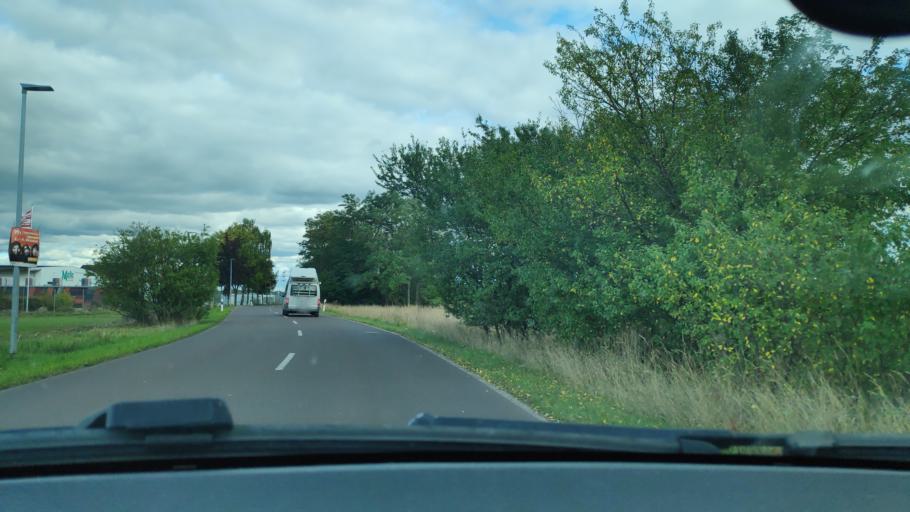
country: DE
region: Saxony-Anhalt
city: Biederitz
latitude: 52.1544
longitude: 11.7330
